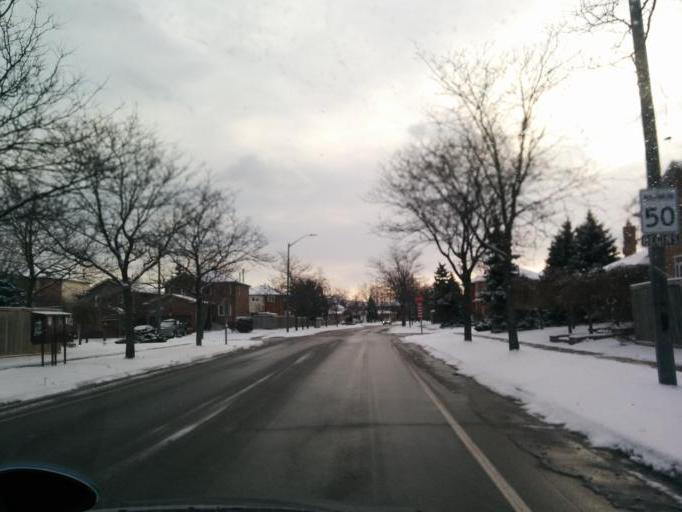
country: CA
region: Ontario
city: Mississauga
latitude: 43.5499
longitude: -79.7087
